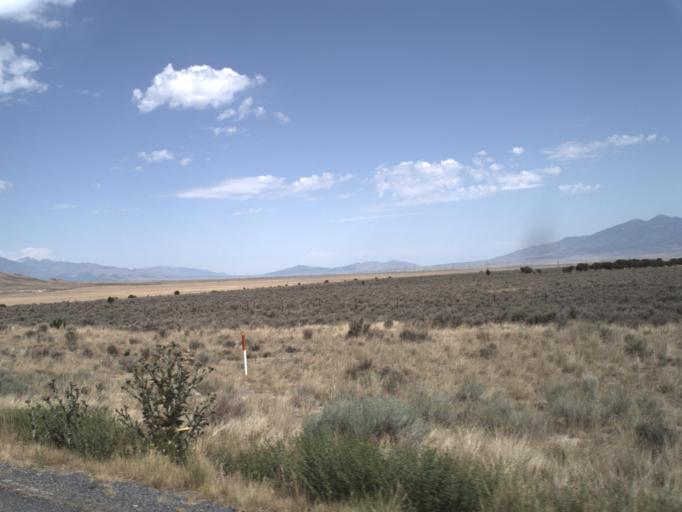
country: US
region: Utah
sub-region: Utah County
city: Eagle Mountain
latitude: 40.0681
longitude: -112.3268
